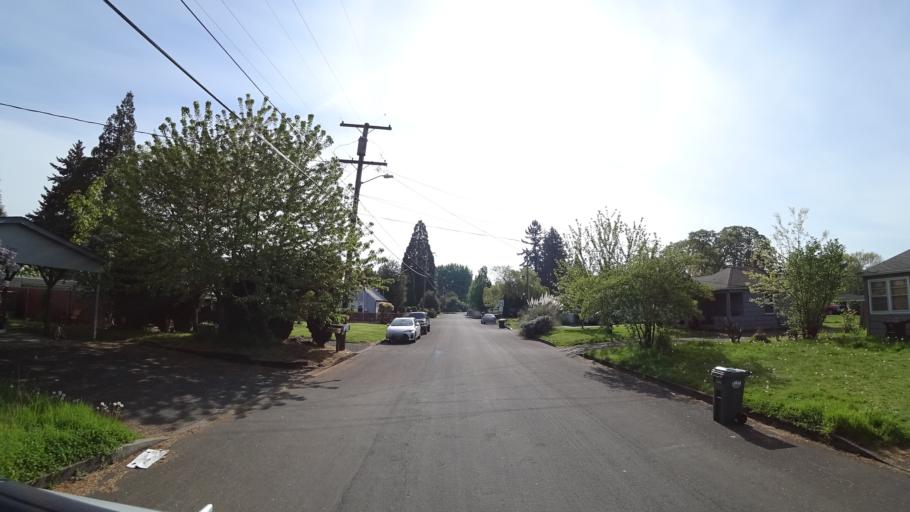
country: US
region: Oregon
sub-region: Washington County
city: Hillsboro
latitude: 45.5237
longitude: -122.9718
